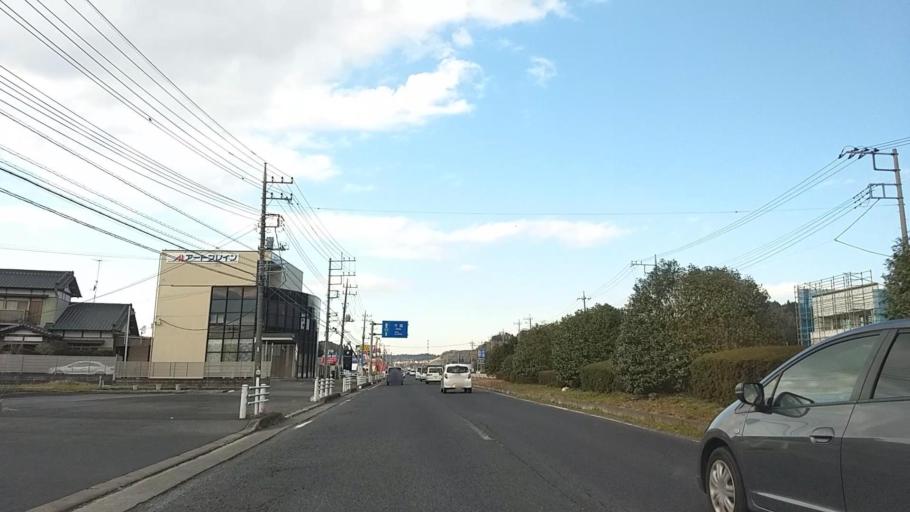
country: JP
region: Chiba
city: Togane
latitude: 35.5610
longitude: 140.3400
